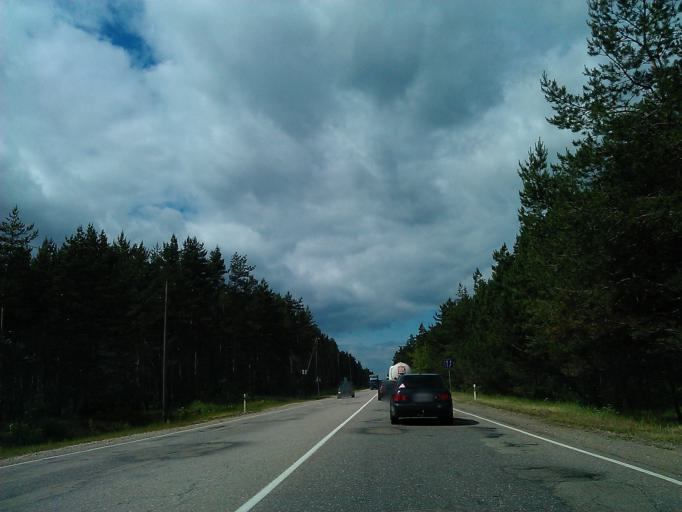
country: LV
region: Babite
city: Pinki
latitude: 56.9643
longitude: 23.8632
